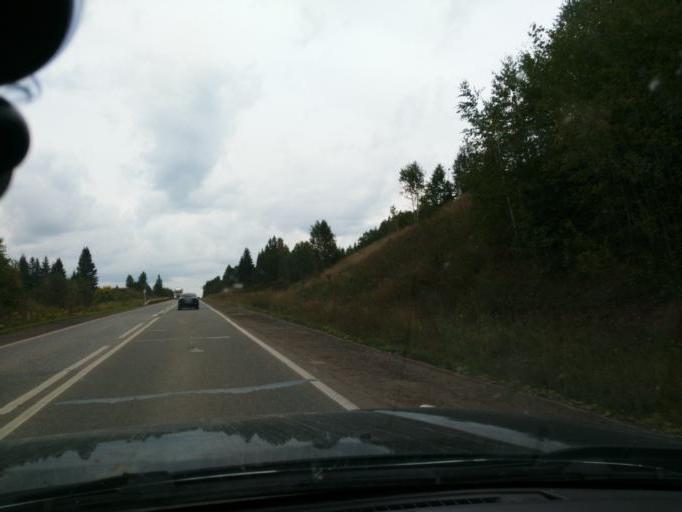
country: RU
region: Perm
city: Chernushka
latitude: 56.7085
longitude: 56.1823
